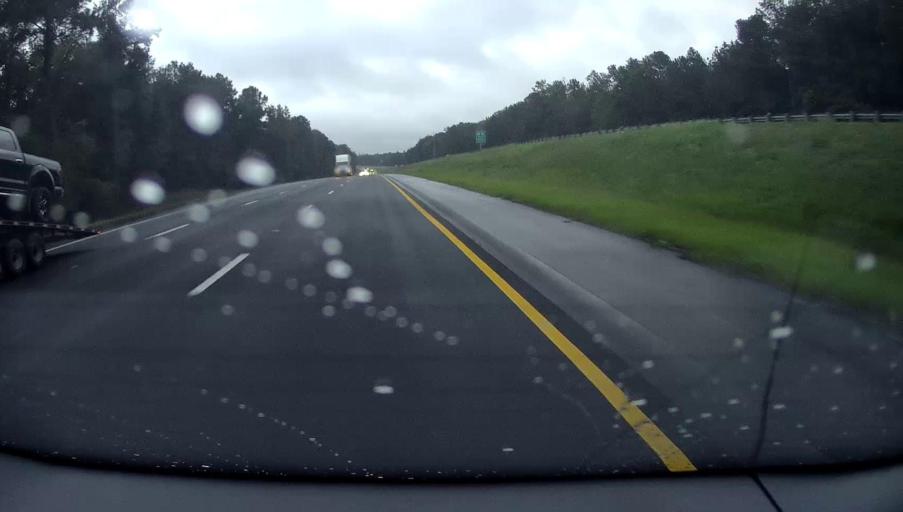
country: US
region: Georgia
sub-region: Bibb County
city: West Point
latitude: 32.7917
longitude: -83.7191
